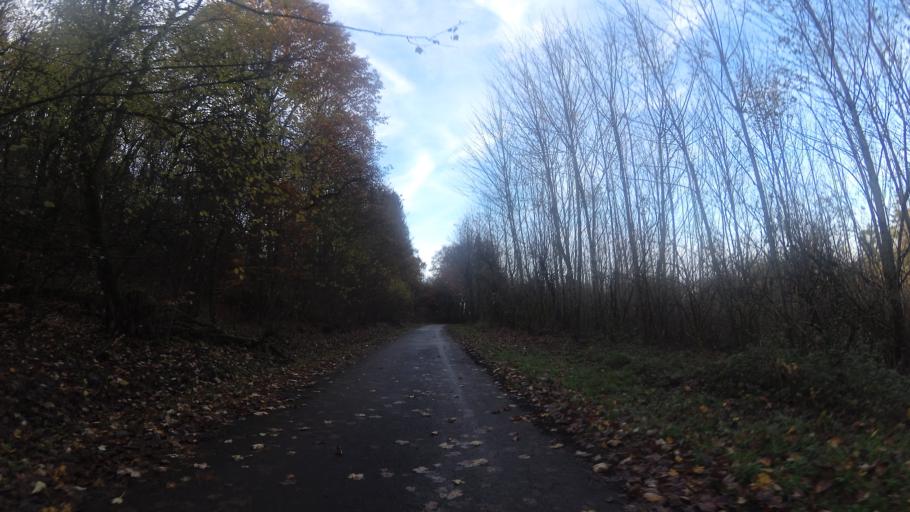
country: DE
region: Saarland
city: Freisen
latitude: 49.5432
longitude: 7.2526
